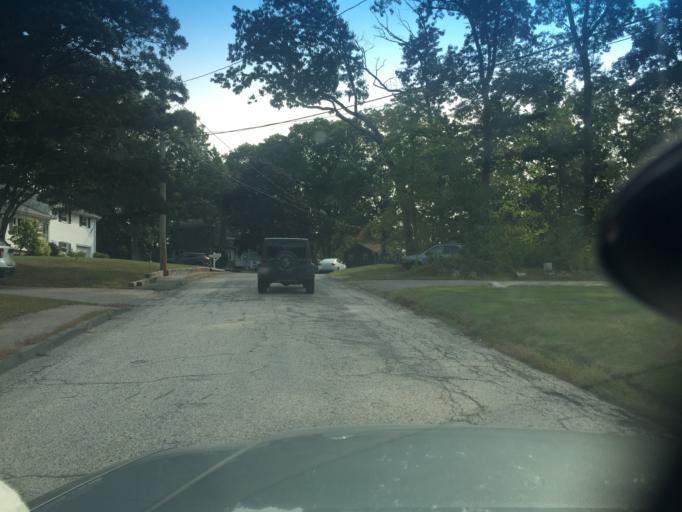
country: US
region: Massachusetts
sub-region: Norfolk County
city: Bellingham
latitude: 42.1180
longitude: -71.4747
